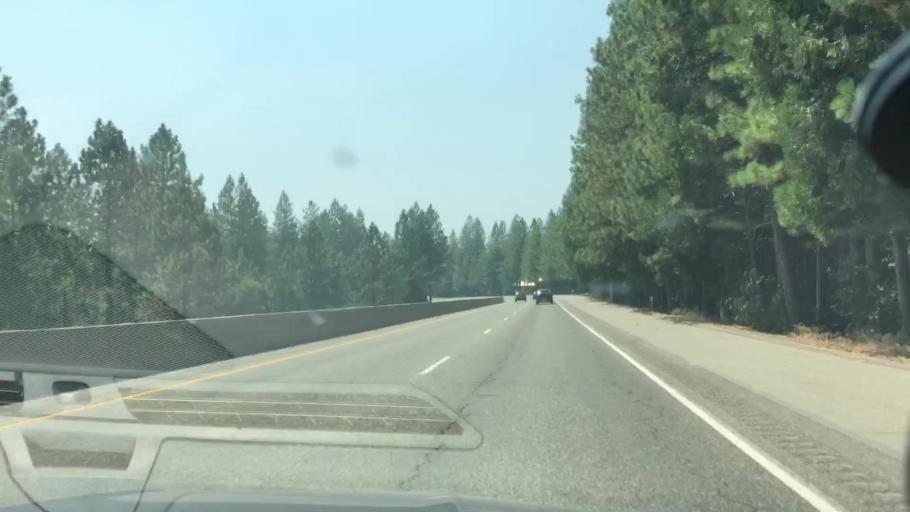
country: US
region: California
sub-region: El Dorado County
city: Camino
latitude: 38.7440
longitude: -120.6551
